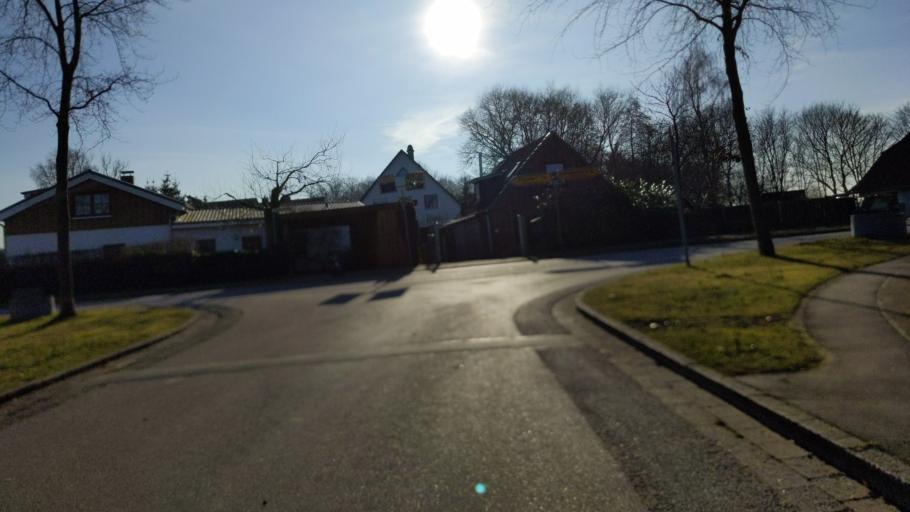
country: DE
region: Schleswig-Holstein
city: Ahrensbok
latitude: 54.0164
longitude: 10.6448
